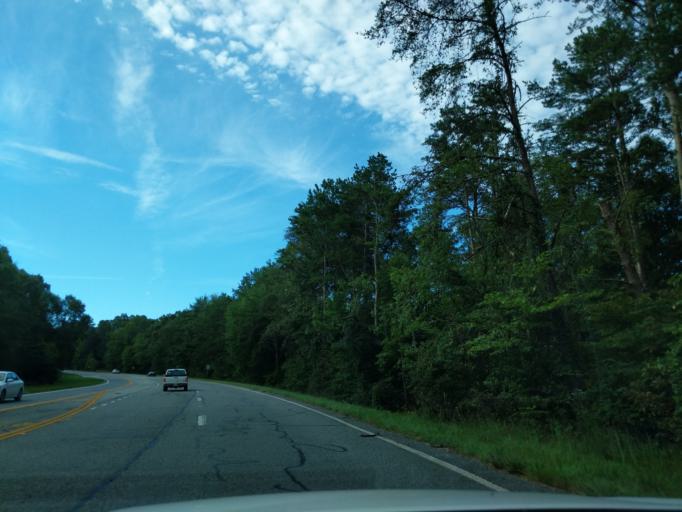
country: US
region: Georgia
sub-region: Fannin County
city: McCaysville
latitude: 34.9401
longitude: -84.3763
